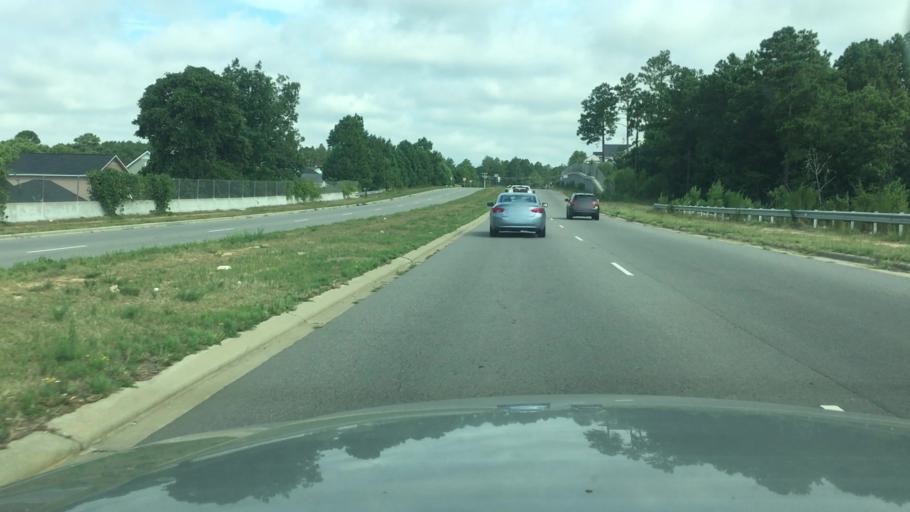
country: US
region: North Carolina
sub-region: Cumberland County
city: Hope Mills
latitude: 34.9713
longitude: -78.9169
